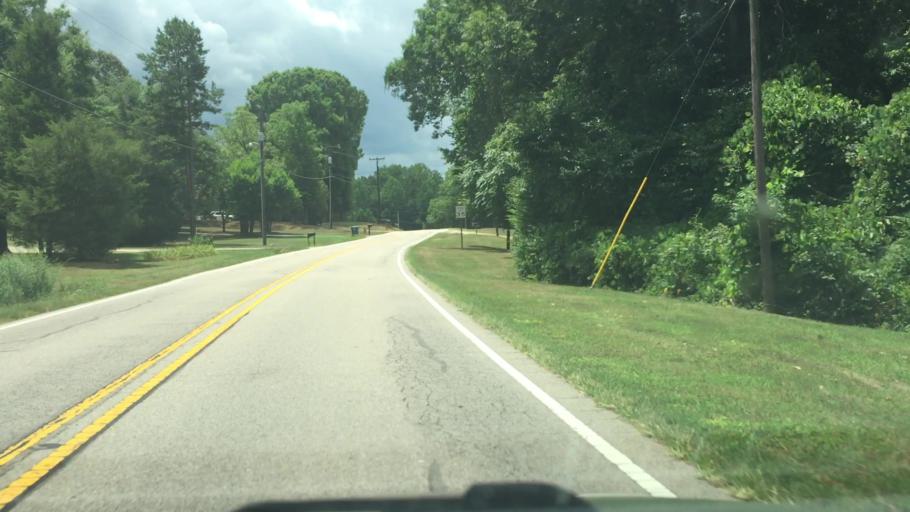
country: US
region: North Carolina
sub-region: Rowan County
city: Enochville
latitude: 35.4982
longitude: -80.6664
